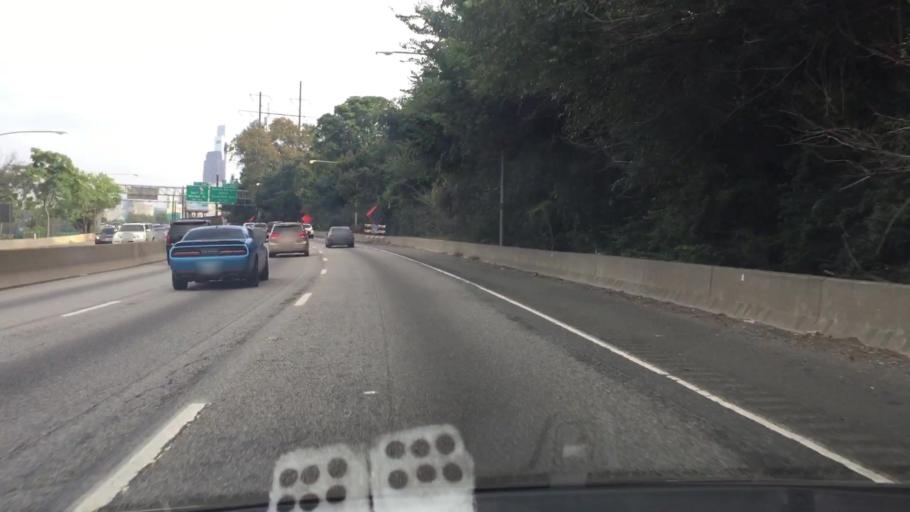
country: US
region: Pennsylvania
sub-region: Philadelphia County
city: Philadelphia
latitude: 39.9690
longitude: -75.1920
